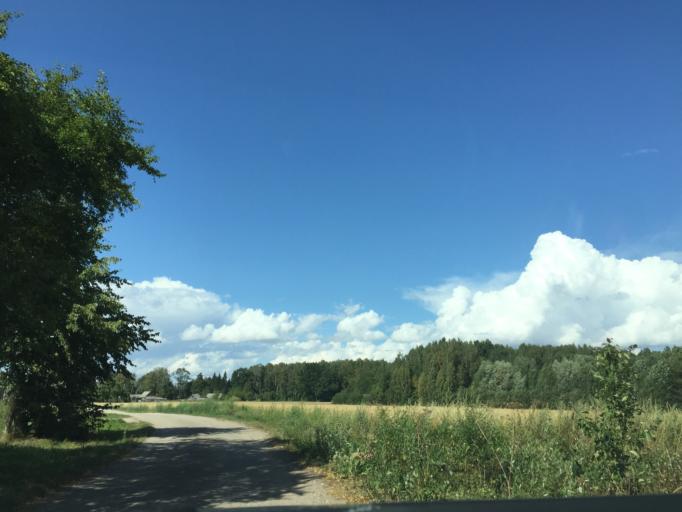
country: LT
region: Siauliu apskritis
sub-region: Joniskis
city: Joniskis
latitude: 56.3363
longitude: 23.5590
